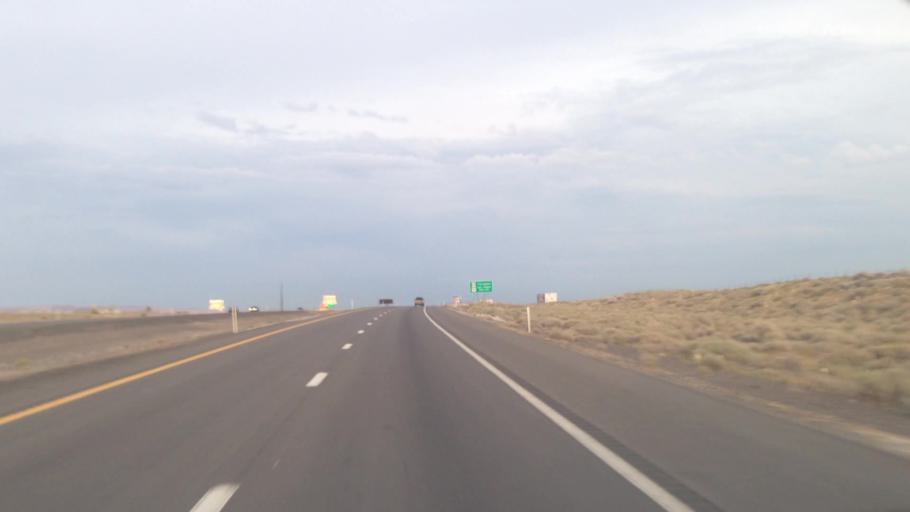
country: US
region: Nevada
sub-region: Lyon County
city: Fernley
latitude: 39.6179
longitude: -119.2804
